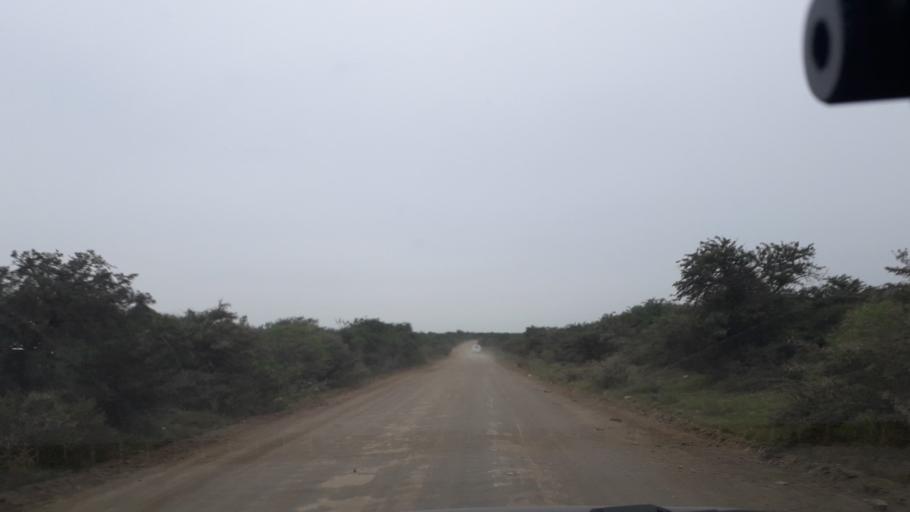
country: ZA
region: Eastern Cape
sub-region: Buffalo City Metropolitan Municipality
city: Bhisho
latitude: -32.7912
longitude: 27.3318
